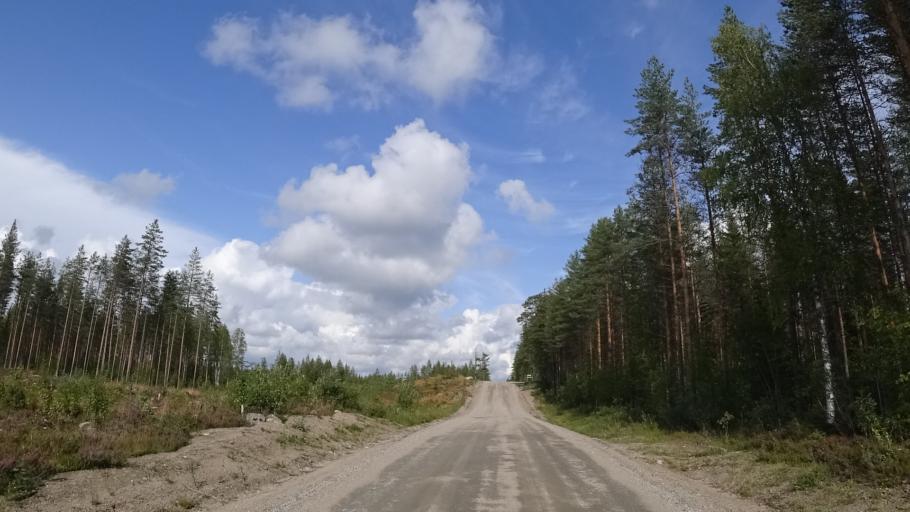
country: FI
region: North Karelia
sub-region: Pielisen Karjala
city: Lieksa
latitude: 63.5731
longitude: 30.1159
